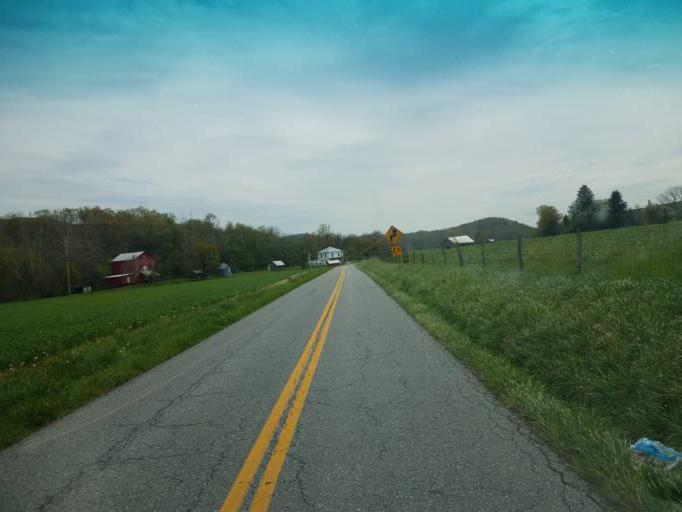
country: US
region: Virginia
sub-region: Smyth County
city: Atkins
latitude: 36.7726
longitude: -81.4384
